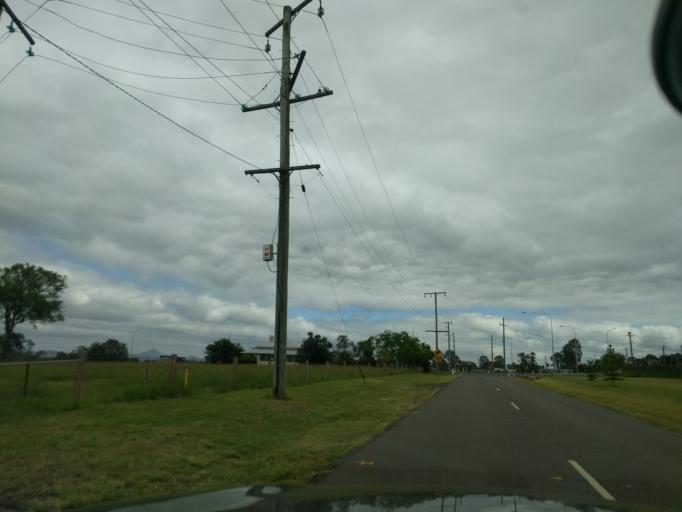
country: AU
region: Queensland
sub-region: Logan
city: Cedar Vale
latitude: -27.9807
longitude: 152.9937
